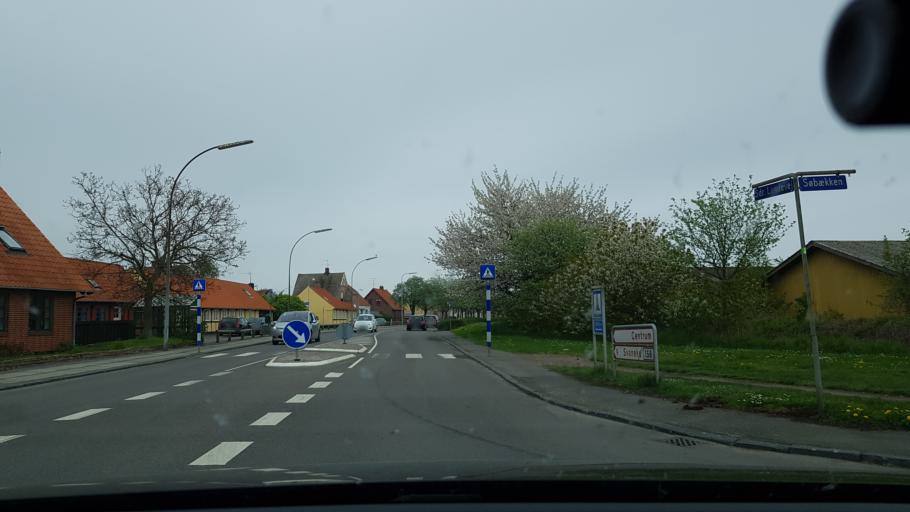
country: DK
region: Capital Region
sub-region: Bornholm Kommune
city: Nexo
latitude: 55.0574
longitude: 15.1281
